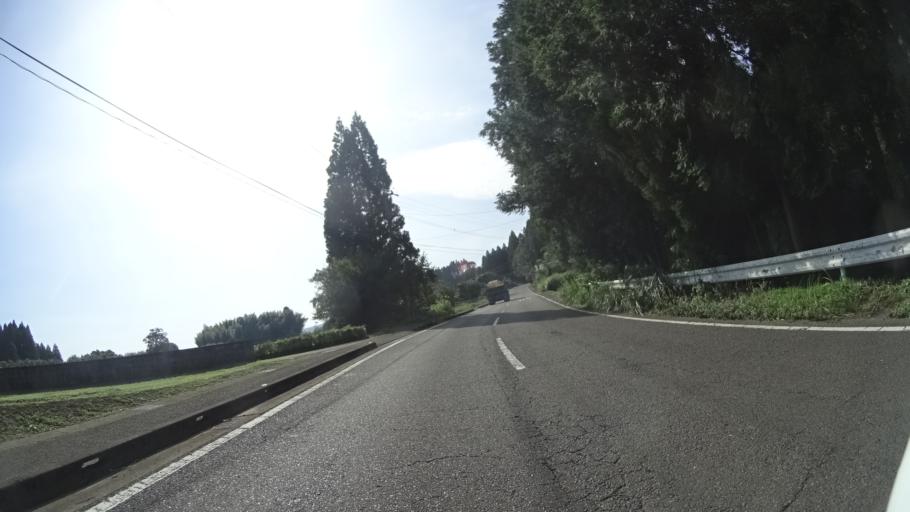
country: JP
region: Miyazaki
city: Kobayashi
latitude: 32.0360
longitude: 130.8220
